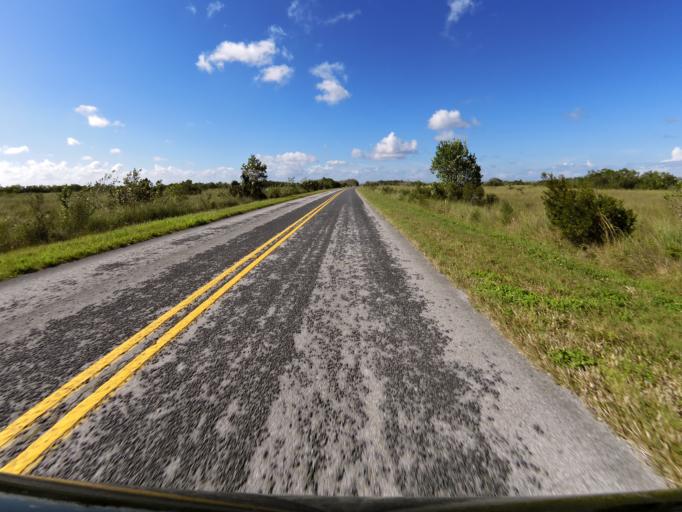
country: US
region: Florida
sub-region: Miami-Dade County
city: Florida City
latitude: 25.4329
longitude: -80.7431
